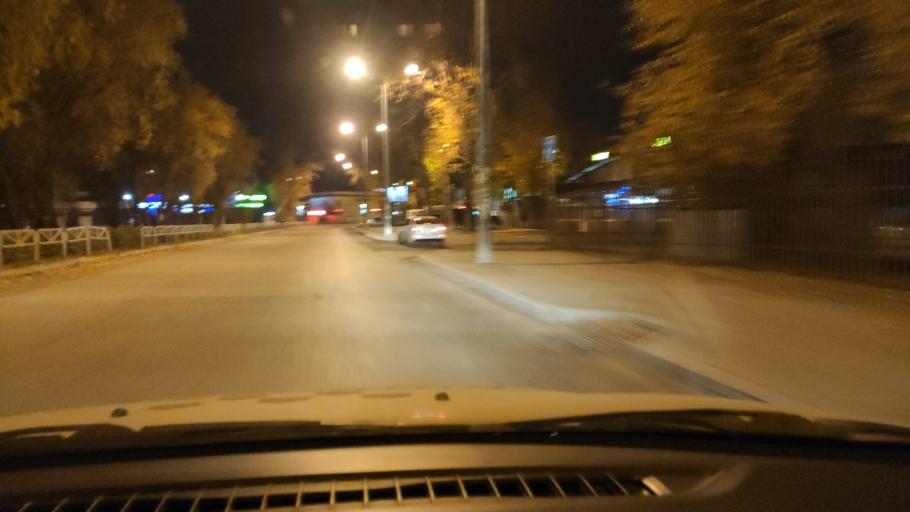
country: RU
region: Perm
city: Perm
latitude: 57.9673
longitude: 56.2643
